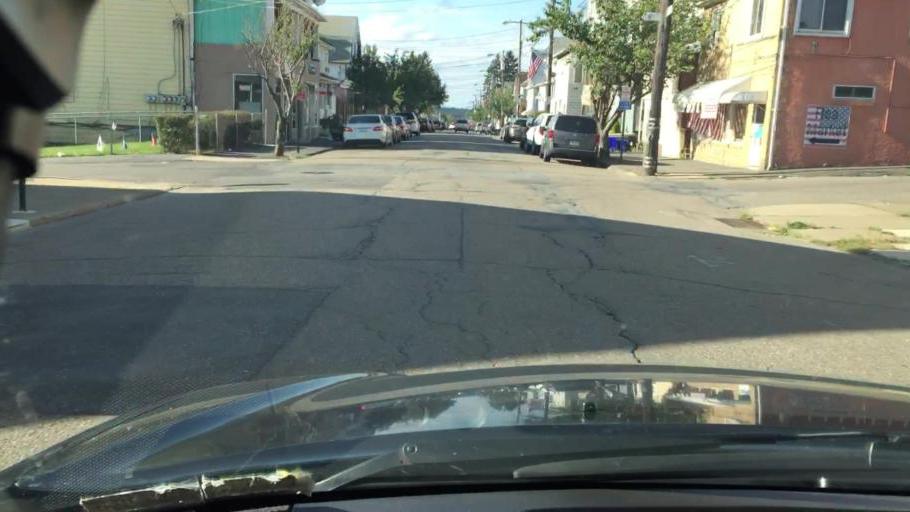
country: US
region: Pennsylvania
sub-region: Luzerne County
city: Hazleton
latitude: 40.9637
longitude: -75.9789
